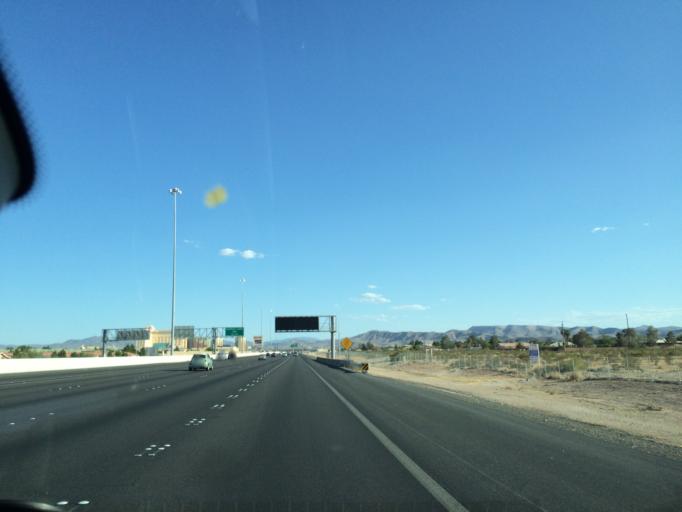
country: US
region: Nevada
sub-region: Clark County
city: Enterprise
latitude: 36.0266
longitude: -115.1810
